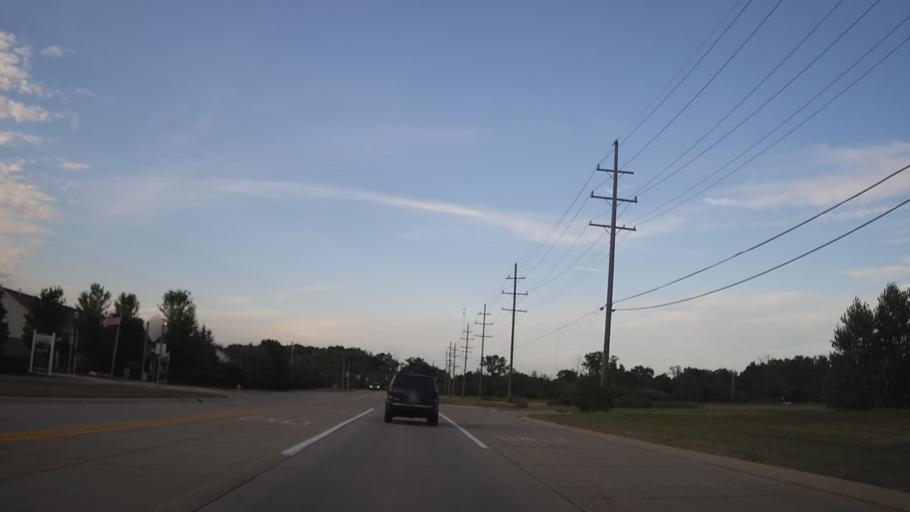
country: US
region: Michigan
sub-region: Macomb County
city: Clinton
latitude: 42.6008
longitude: -82.9156
